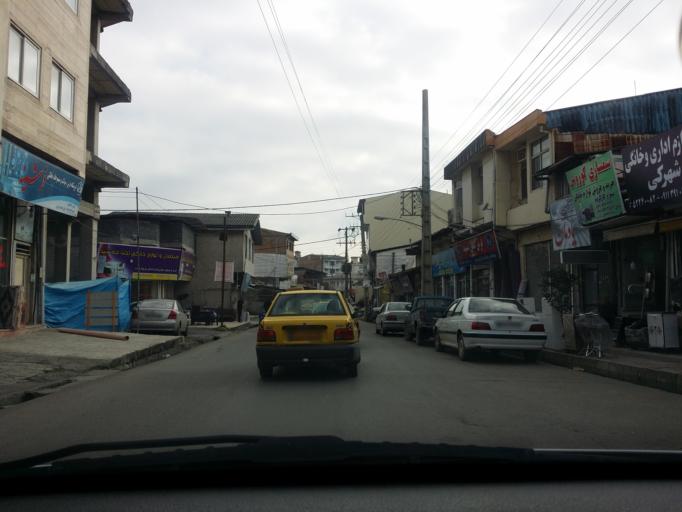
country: IR
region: Mazandaran
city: Chalus
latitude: 36.6573
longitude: 51.4121
